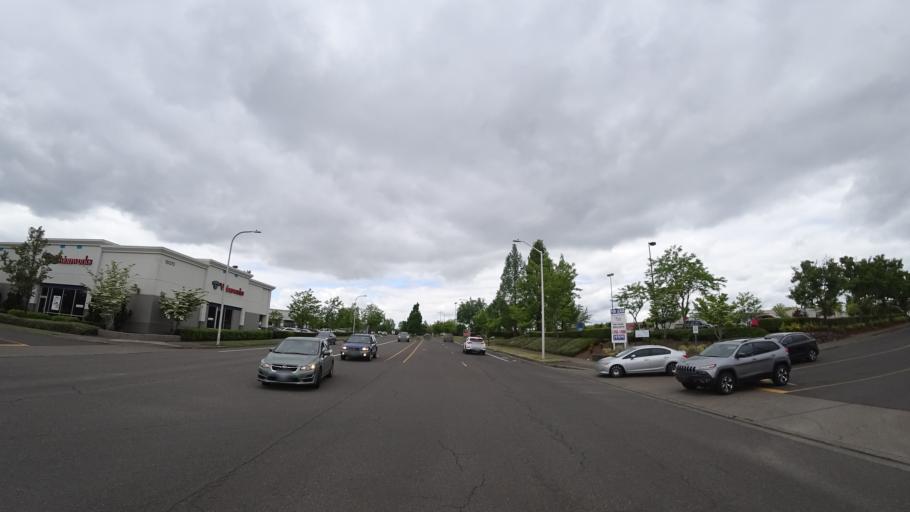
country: US
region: Oregon
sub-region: Washington County
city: Rockcreek
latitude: 45.5367
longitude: -122.8630
